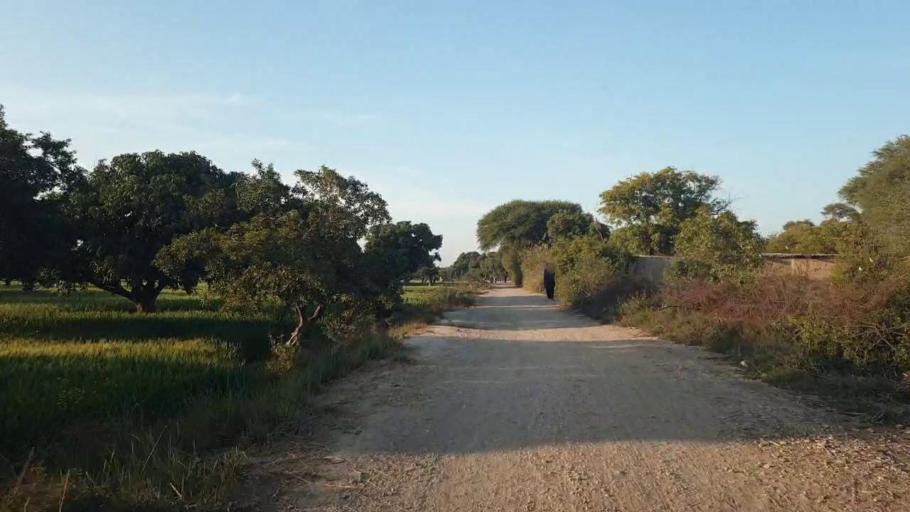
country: PK
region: Sindh
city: Chambar
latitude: 25.2760
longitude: 68.7744
